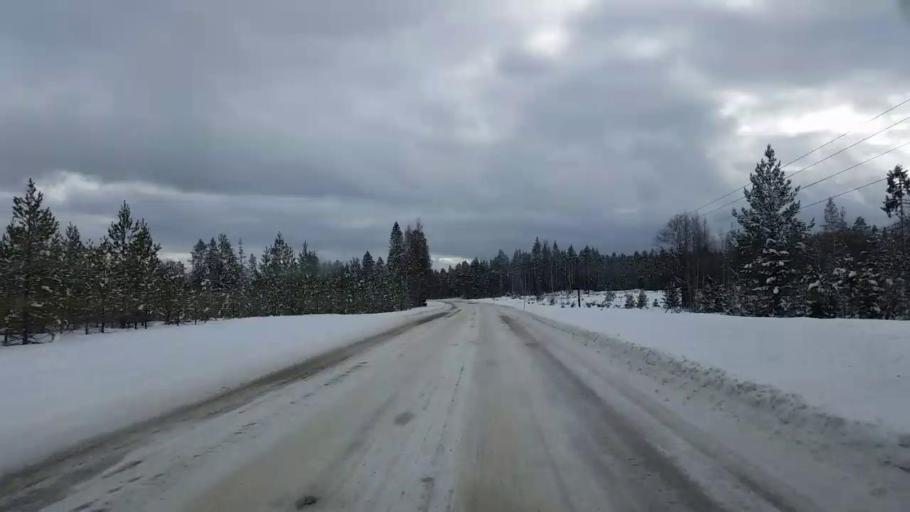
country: SE
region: Jaemtland
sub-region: Harjedalens Kommun
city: Sveg
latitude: 62.1045
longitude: 15.0674
